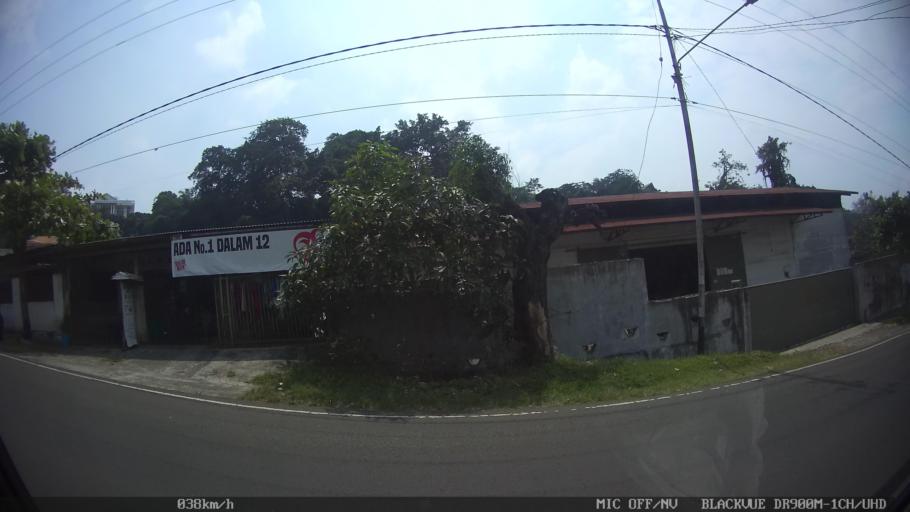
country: ID
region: Lampung
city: Bandarlampung
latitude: -5.4337
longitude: 105.2734
